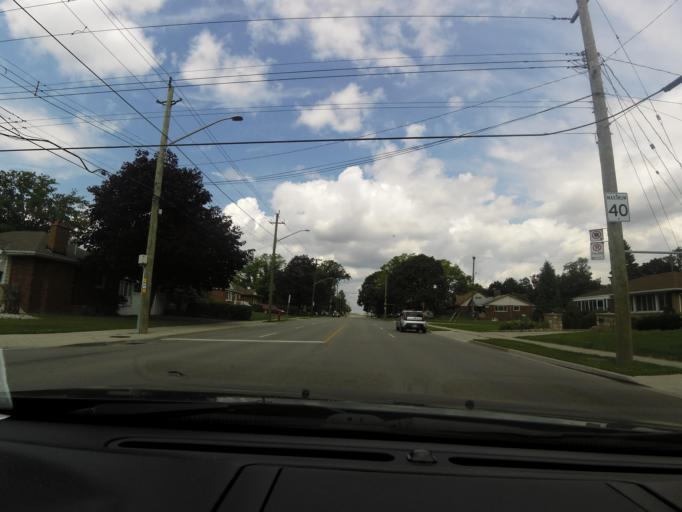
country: CA
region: Ontario
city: Hamilton
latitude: 43.2298
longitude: -79.8276
